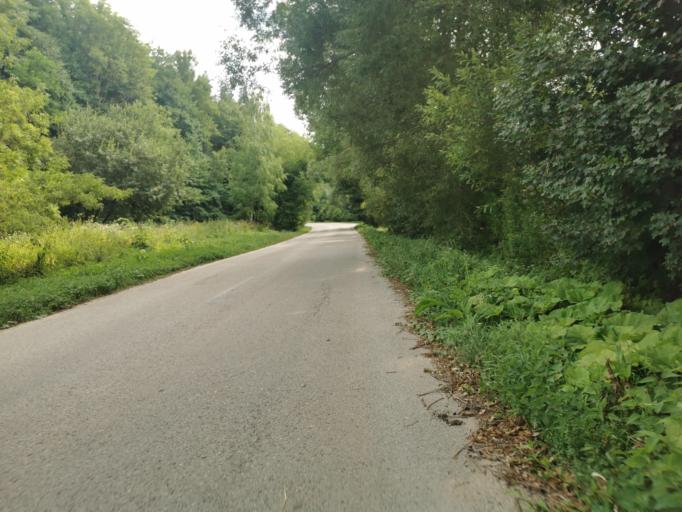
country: SK
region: Trenciansky
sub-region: Okres Myjava
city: Myjava
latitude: 48.7399
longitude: 17.5133
